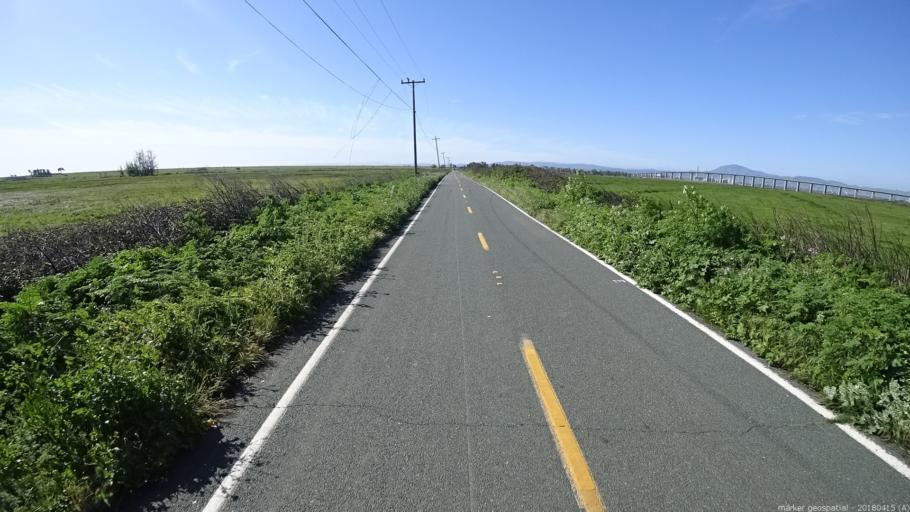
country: US
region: California
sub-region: Contra Costa County
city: Oakley
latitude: 38.0442
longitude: -121.7362
